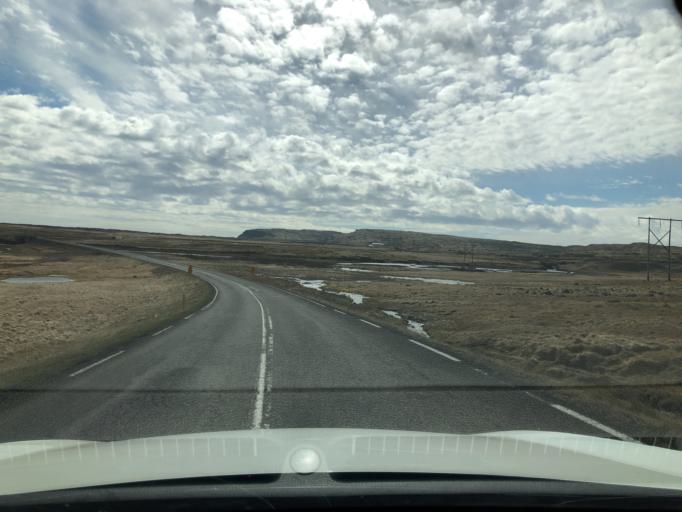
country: IS
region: East
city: Reydarfjoerdur
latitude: 64.6939
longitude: -14.3801
